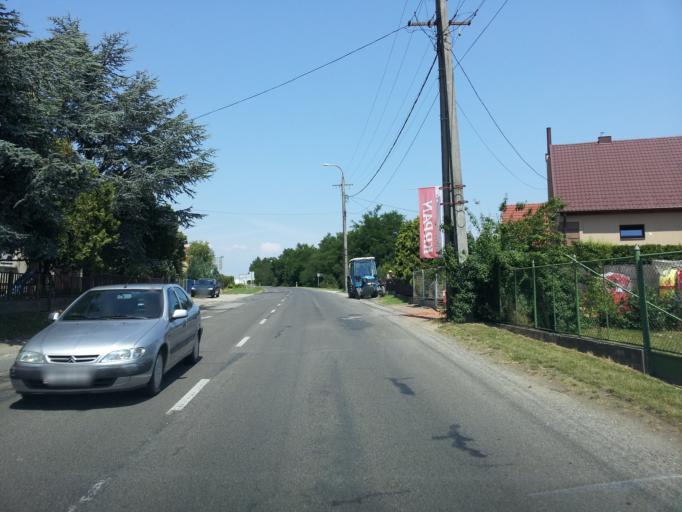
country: HU
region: Zala
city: Zalaegerszeg
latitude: 46.8652
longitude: 16.7993
